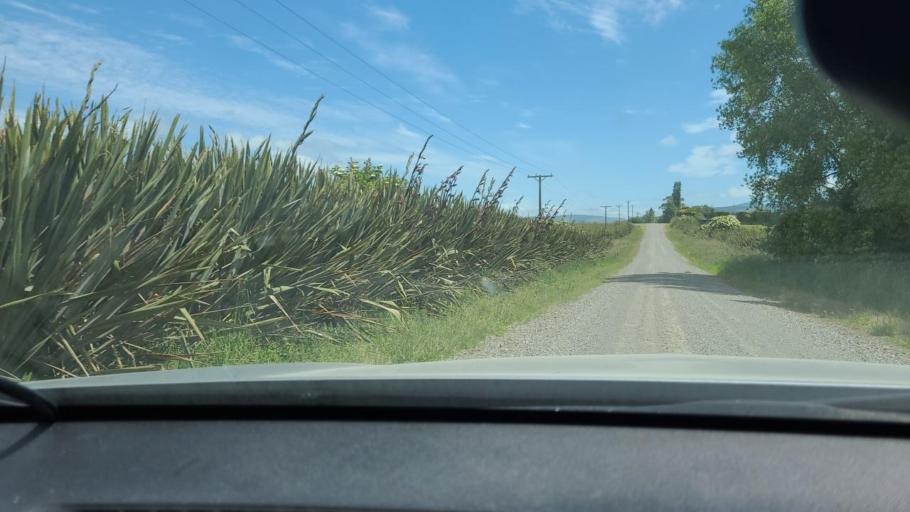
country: NZ
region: Southland
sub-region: Southland District
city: Winton
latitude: -46.0298
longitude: 168.0524
